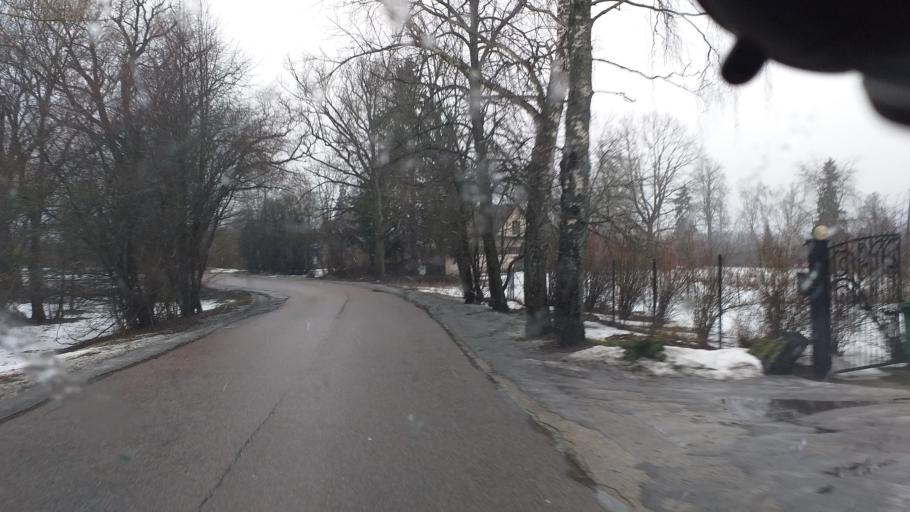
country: LV
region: Riga
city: Daugavgriva
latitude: 56.9868
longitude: 24.0151
